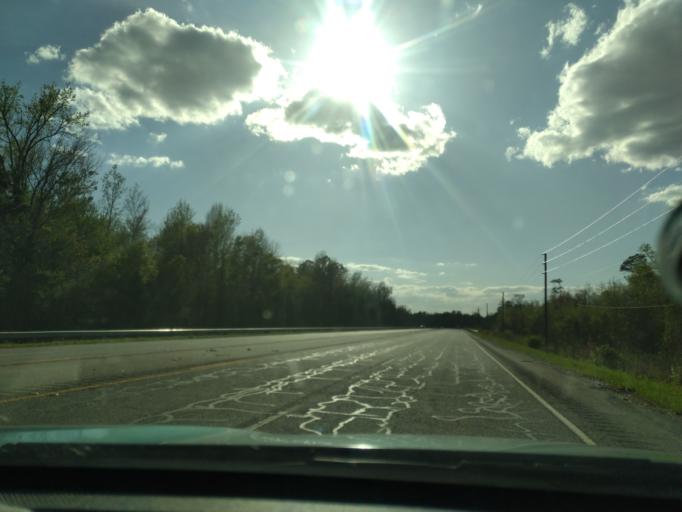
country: US
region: South Carolina
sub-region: Williamsburg County
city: Kingstree
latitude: 33.6577
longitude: -79.8679
